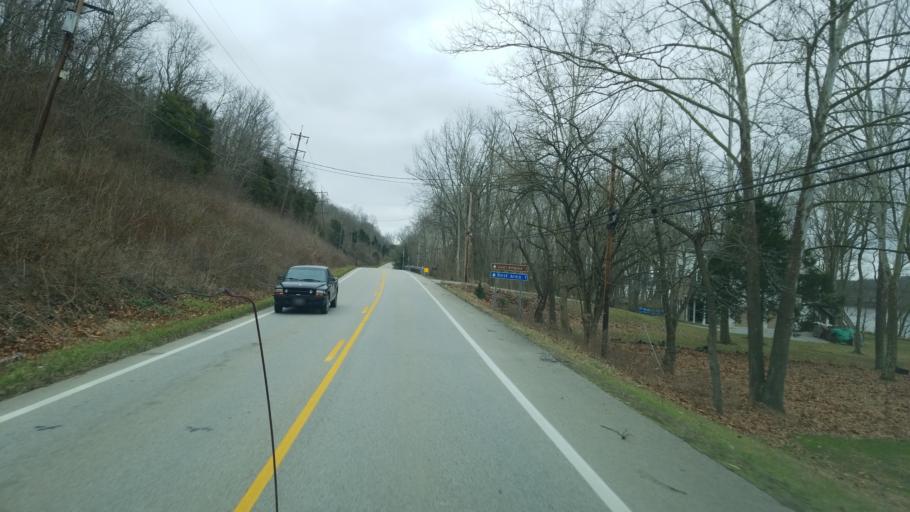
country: US
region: Ohio
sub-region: Clermont County
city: New Richmond
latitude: 38.9063
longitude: -84.2433
